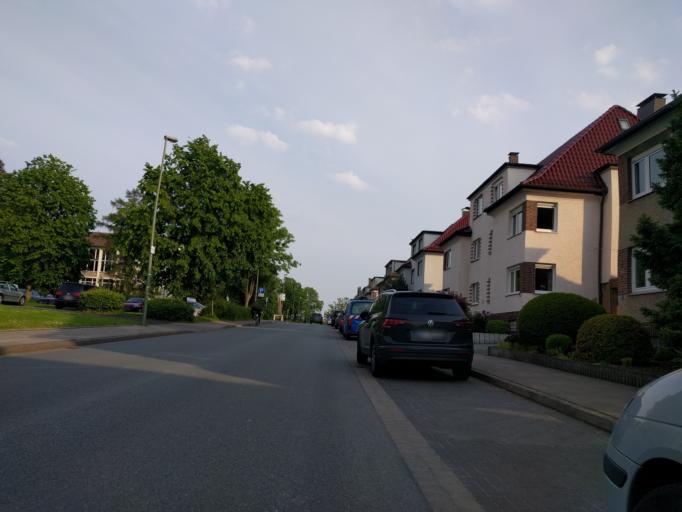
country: DE
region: North Rhine-Westphalia
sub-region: Regierungsbezirk Detmold
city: Bielefeld
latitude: 52.0425
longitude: 8.5145
